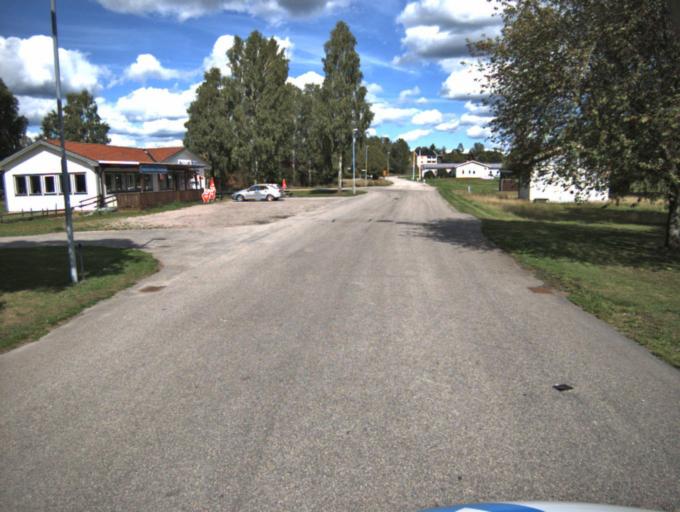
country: SE
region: Vaestra Goetaland
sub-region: Ulricehamns Kommun
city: Ulricehamn
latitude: 57.9317
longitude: 13.4940
